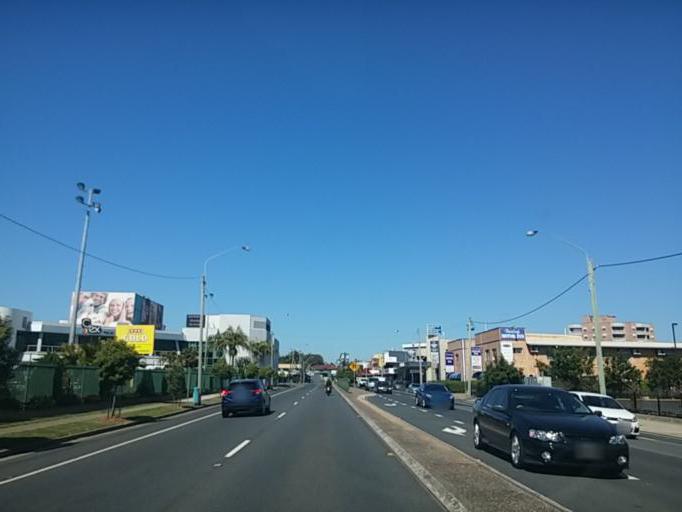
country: AU
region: New South Wales
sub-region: Coffs Harbour
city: Coffs Harbour
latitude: -30.2944
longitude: 153.1158
